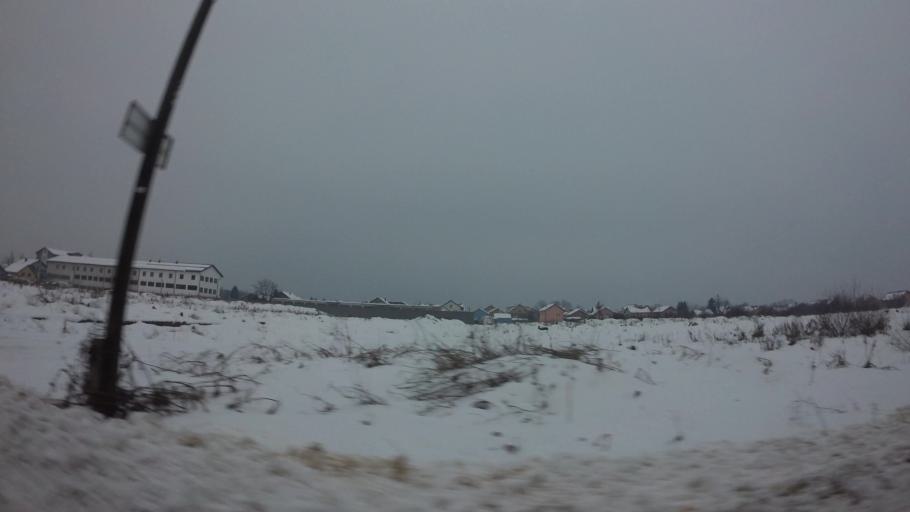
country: BA
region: Federation of Bosnia and Herzegovina
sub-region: Kanton Sarajevo
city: Sarajevo
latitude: 43.8427
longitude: 18.3105
